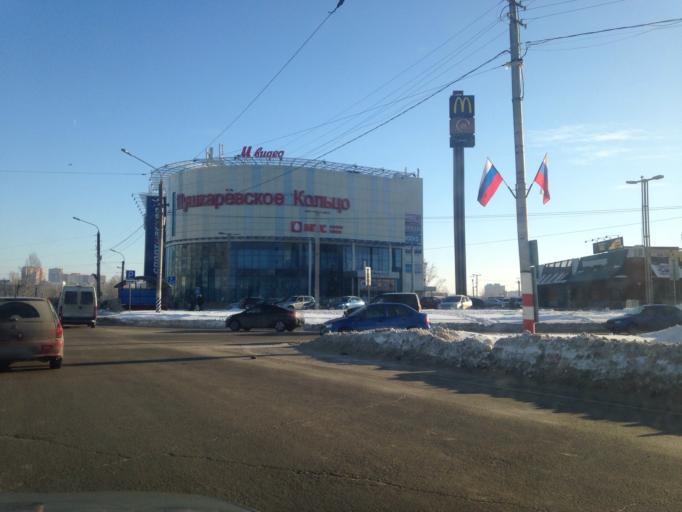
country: RU
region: Ulyanovsk
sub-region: Ulyanovskiy Rayon
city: Ulyanovsk
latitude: 54.3060
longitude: 48.3497
